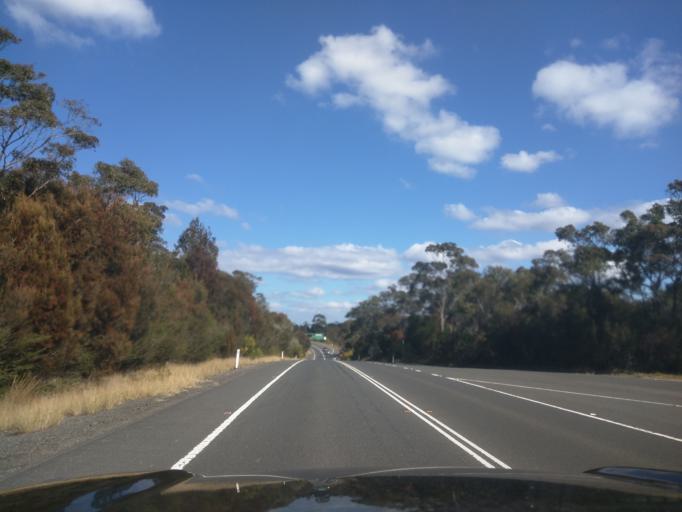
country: AU
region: New South Wales
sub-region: Sutherland Shire
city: Engadine
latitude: -34.0510
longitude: 150.9745
